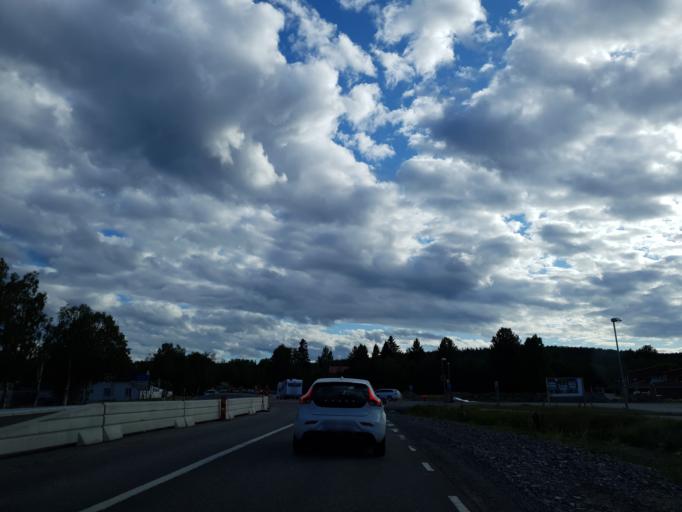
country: SE
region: Vaesternorrland
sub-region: Haernoesands Kommun
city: Haernoesand
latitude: 62.6744
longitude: 17.8406
